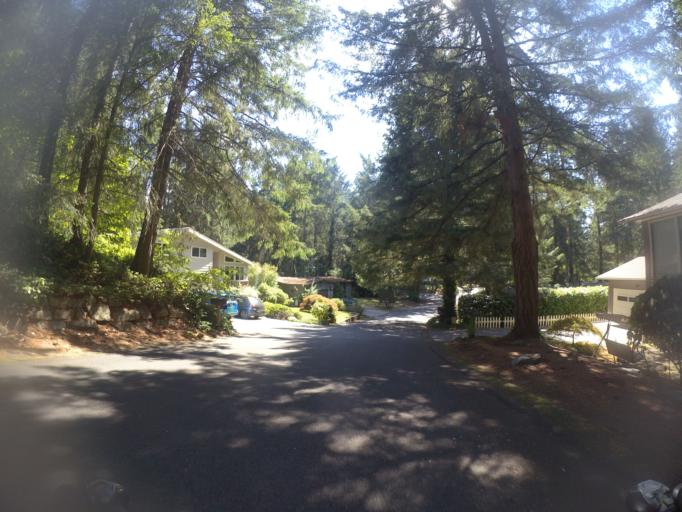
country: US
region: Washington
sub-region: Pierce County
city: University Place
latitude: 47.2170
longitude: -122.5605
